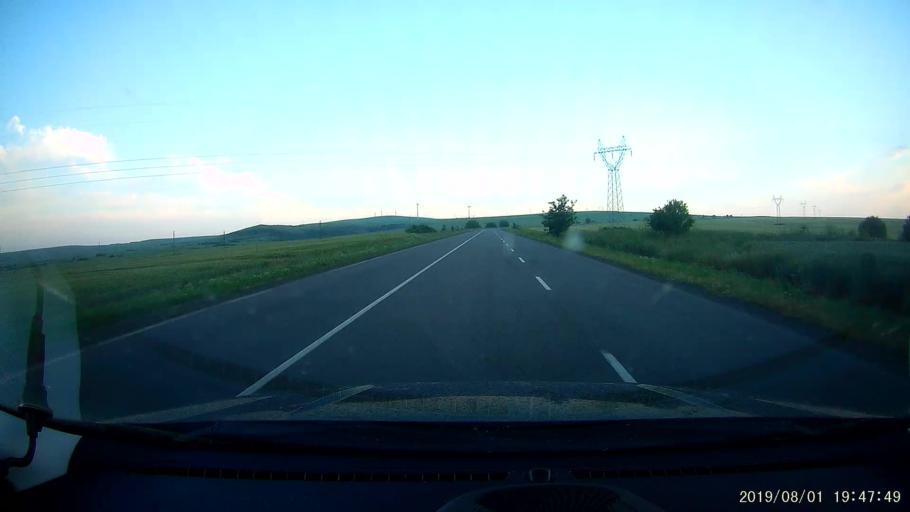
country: BG
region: Burgas
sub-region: Obshtina Karnobat
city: Karnobat
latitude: 42.6461
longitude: 26.9580
